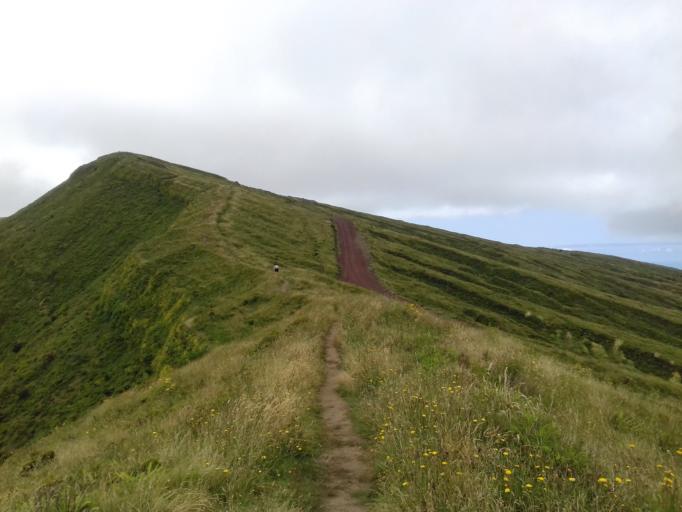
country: PT
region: Azores
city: Ribeira Grande
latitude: 38.5897
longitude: -28.7253
